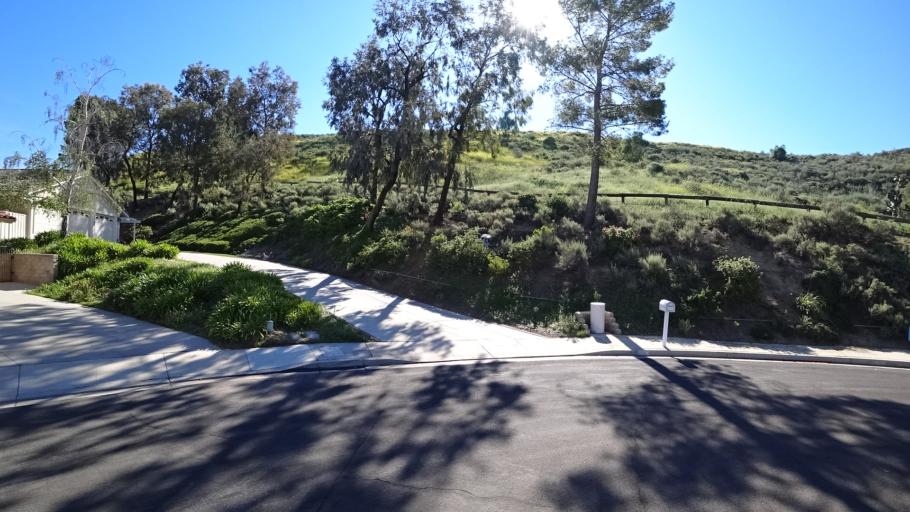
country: US
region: California
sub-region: Ventura County
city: Thousand Oaks
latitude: 34.2253
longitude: -118.8548
